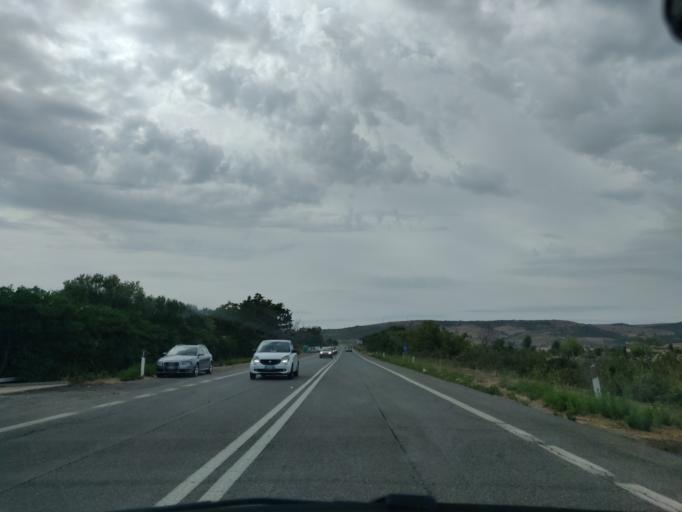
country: IT
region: Latium
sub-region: Citta metropolitana di Roma Capitale
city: Santa Marinella
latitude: 42.0332
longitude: 11.9316
